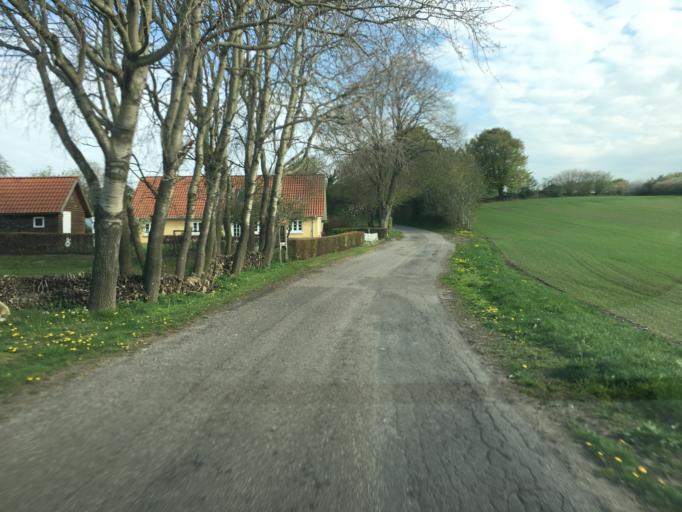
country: DK
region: South Denmark
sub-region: Haderslev Kommune
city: Vojens
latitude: 55.1921
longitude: 9.3900
